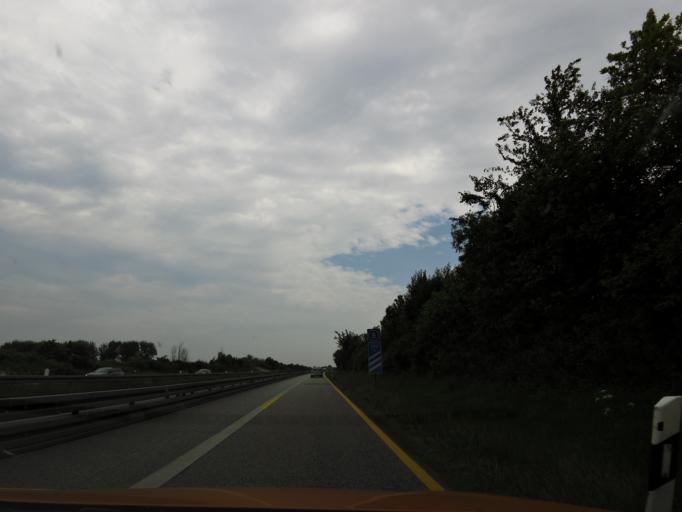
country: DE
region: Mecklenburg-Vorpommern
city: Wismar
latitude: 53.8642
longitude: 11.4271
